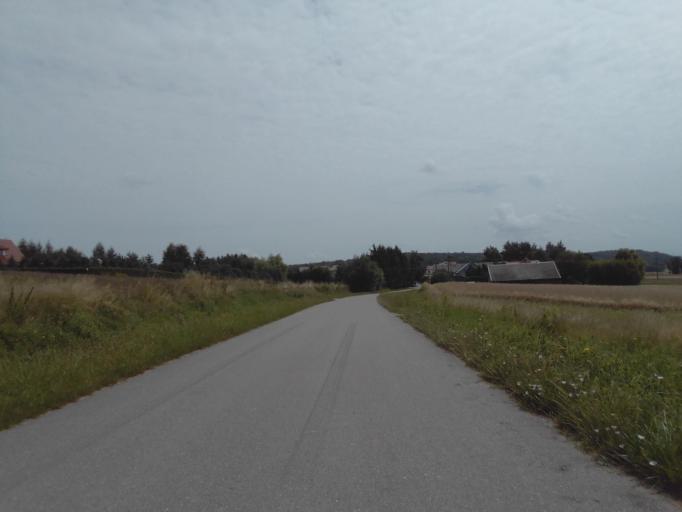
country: PL
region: Subcarpathian Voivodeship
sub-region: Powiat jasielski
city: Tarnowiec
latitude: 49.7762
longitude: 21.6087
